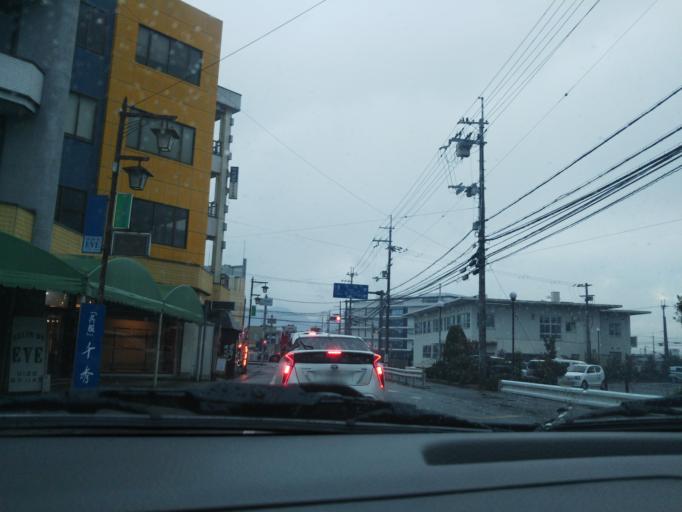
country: JP
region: Shiga Prefecture
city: Minakuchicho-matoba
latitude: 34.9658
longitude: 136.1691
